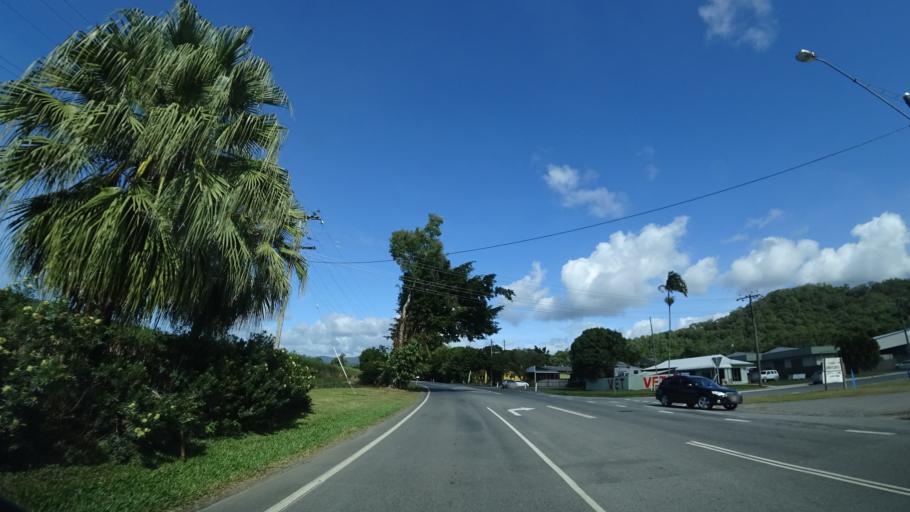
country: AU
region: Queensland
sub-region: Cairns
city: Port Douglas
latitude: -16.4824
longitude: 145.3772
